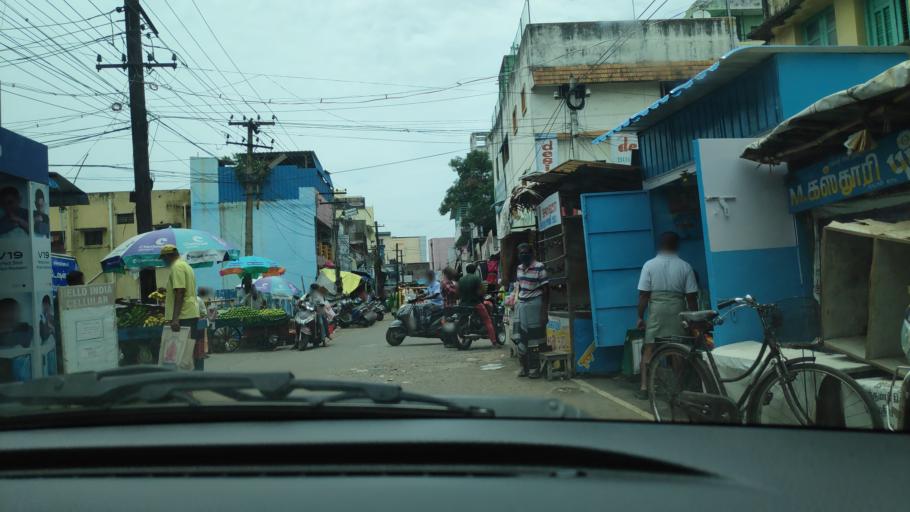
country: IN
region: Tamil Nadu
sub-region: Kancheepuram
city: Pallavaram
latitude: 12.9509
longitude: 80.1440
